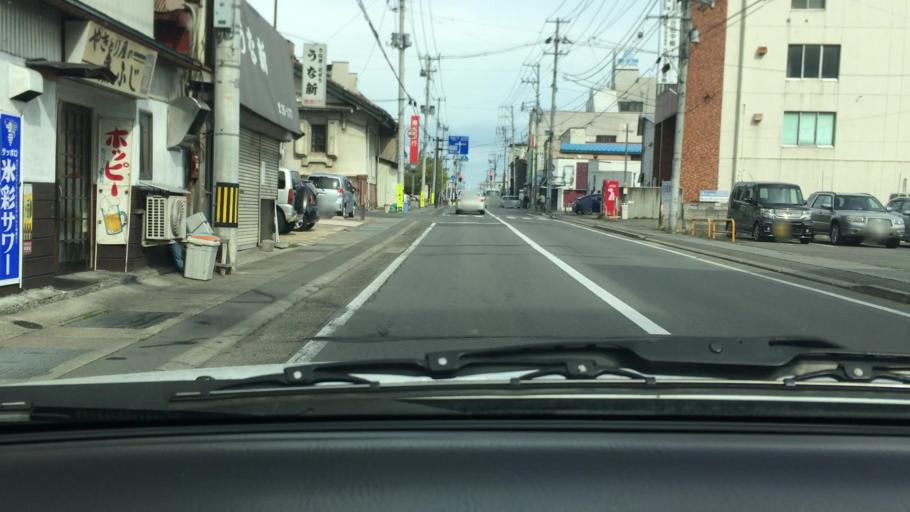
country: JP
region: Aomori
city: Hirosaki
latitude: 40.6019
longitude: 140.4692
